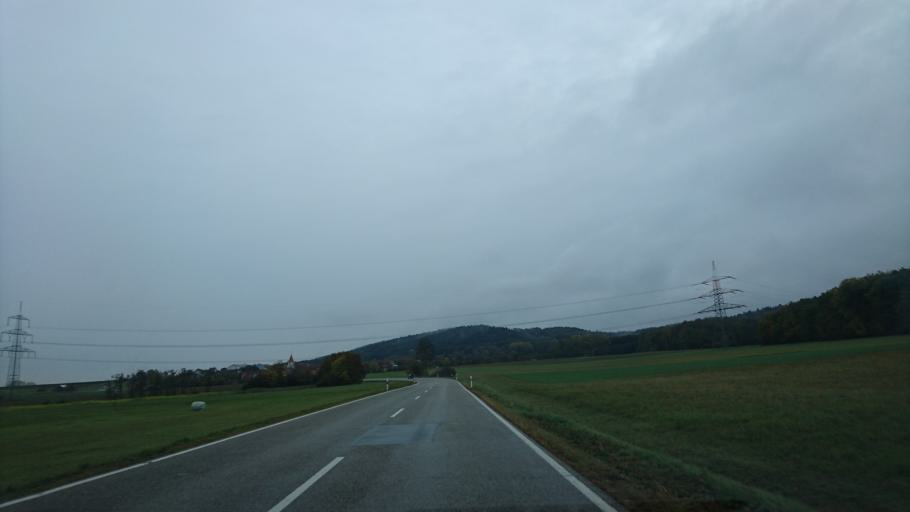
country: DE
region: Bavaria
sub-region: Regierungsbezirk Mittelfranken
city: Bergen
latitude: 49.0849
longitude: 11.0860
